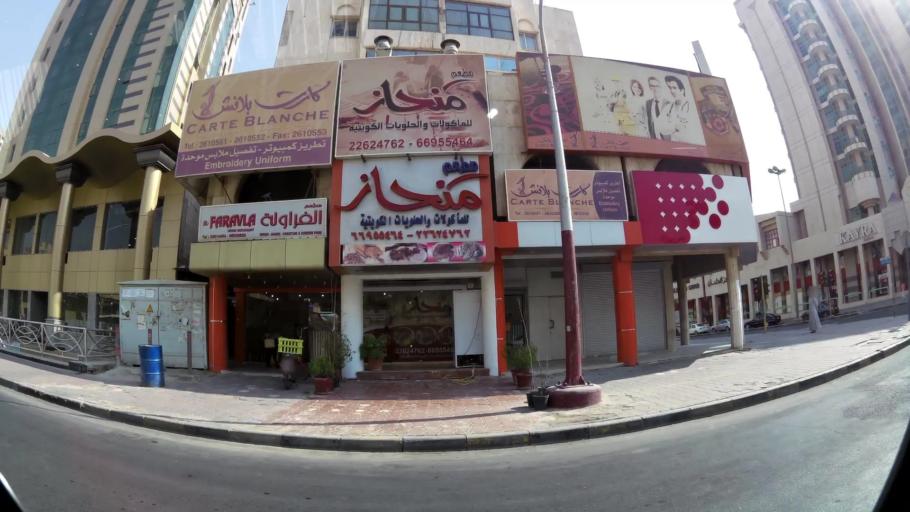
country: KW
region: Muhafazat Hawalli
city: Hawalli
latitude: 29.3434
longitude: 48.0129
